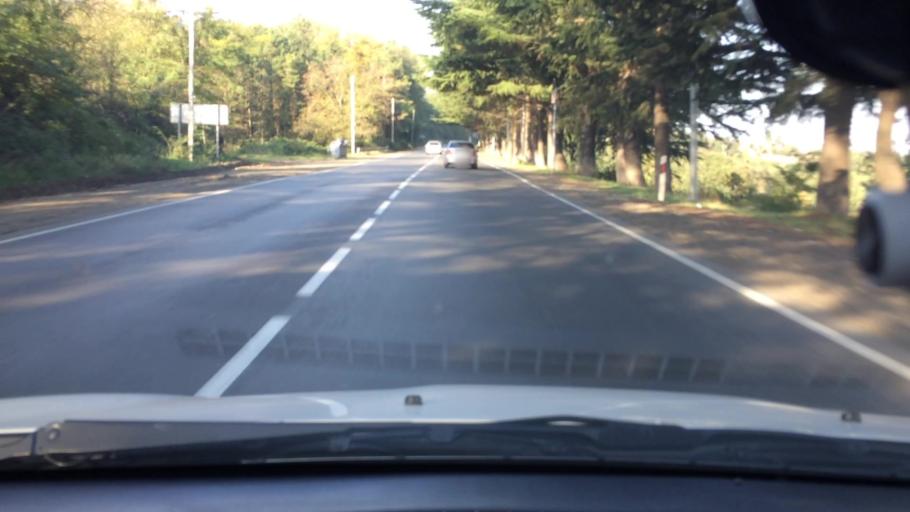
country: GE
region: Imereti
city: Zestap'oni
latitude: 42.1011
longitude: 43.0635
